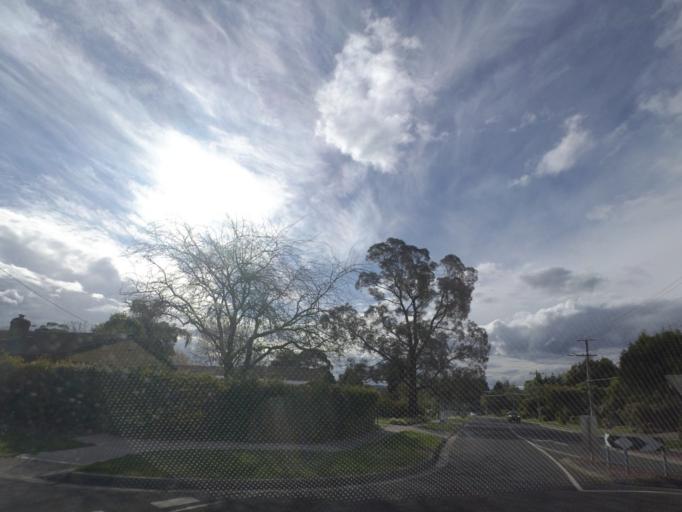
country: AU
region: Victoria
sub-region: Yarra Ranges
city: Lilydale
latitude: -37.7503
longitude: 145.3655
